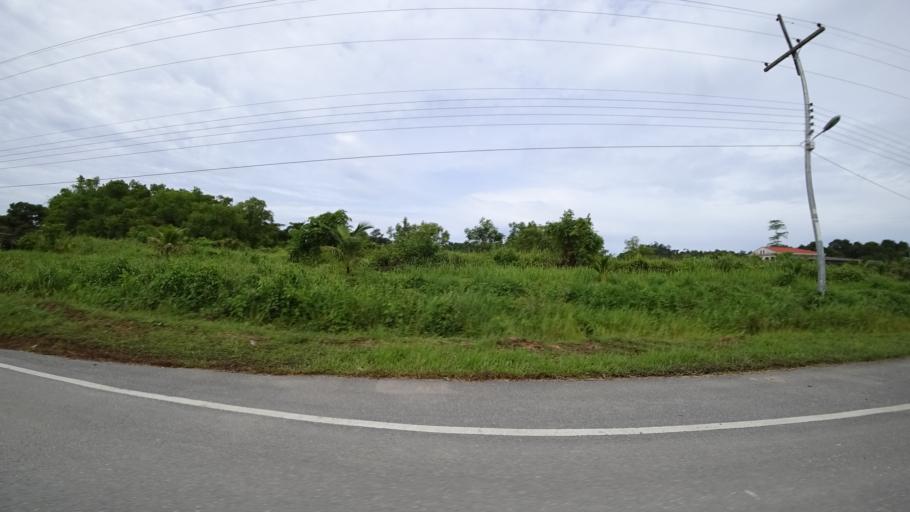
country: MY
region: Sarawak
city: Limbang
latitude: 4.6700
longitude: 114.9852
